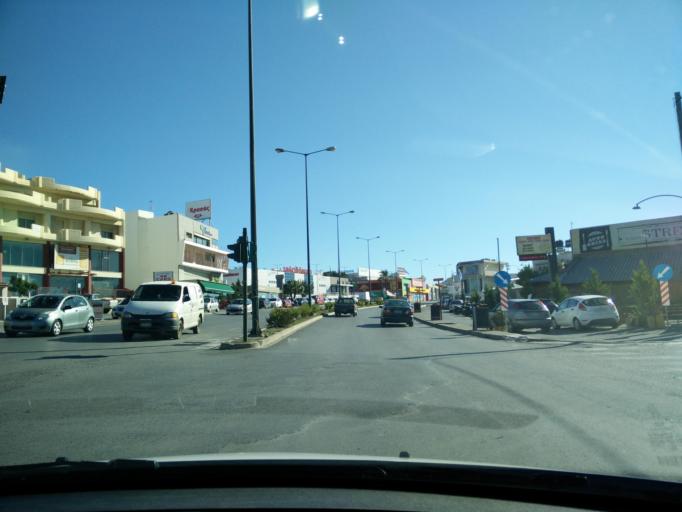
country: GR
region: Crete
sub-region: Nomos Irakleiou
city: Nea Alikarnassos
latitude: 35.3356
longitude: 25.1570
